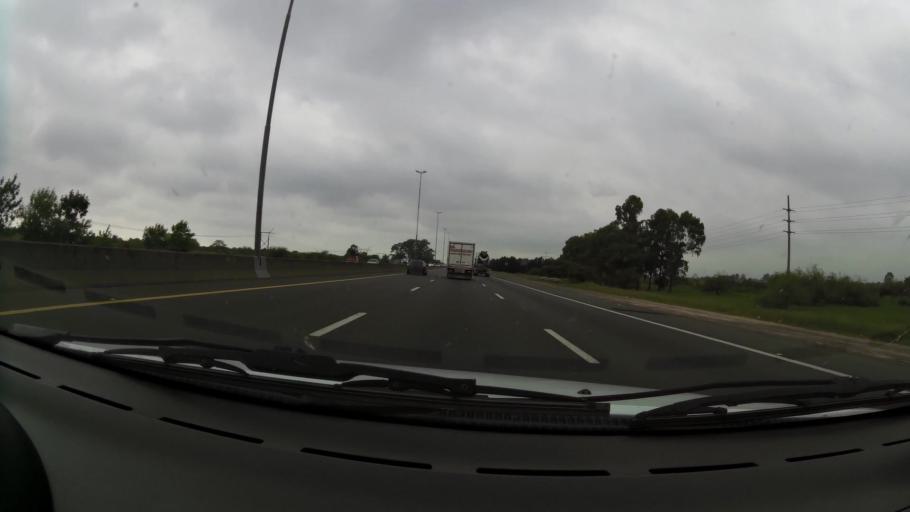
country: AR
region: Buenos Aires
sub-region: Partido de Quilmes
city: Quilmes
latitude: -34.7287
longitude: -58.2211
